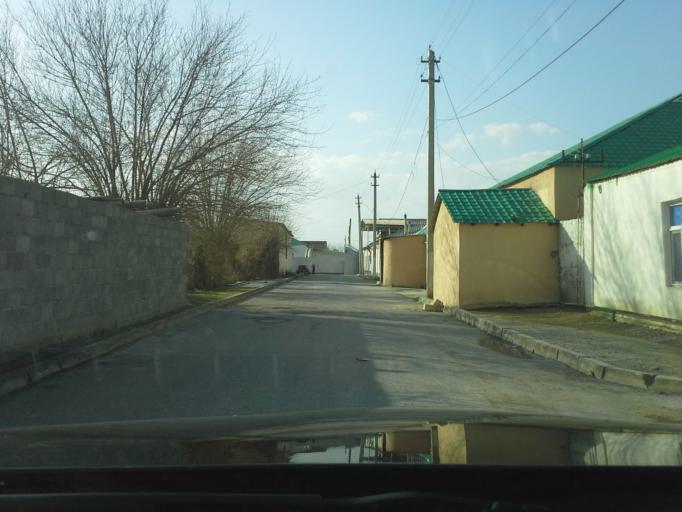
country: TM
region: Ahal
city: Abadan
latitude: 38.0191
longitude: 58.2330
